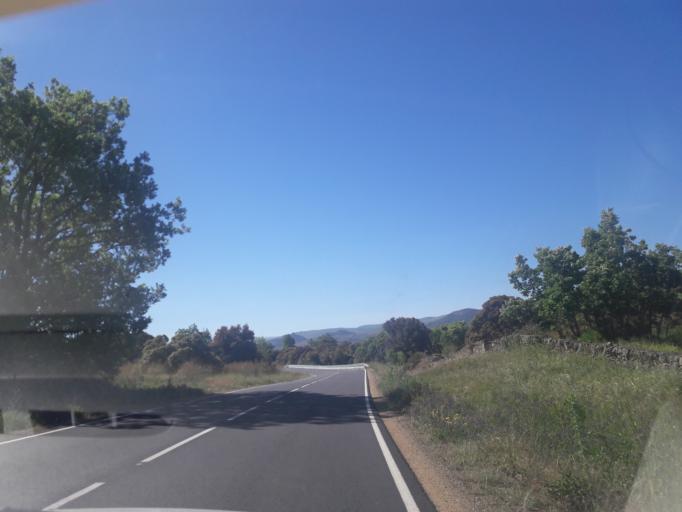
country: ES
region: Castille and Leon
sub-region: Provincia de Salamanca
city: Nava de Bejar
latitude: 40.4873
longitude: -5.6543
